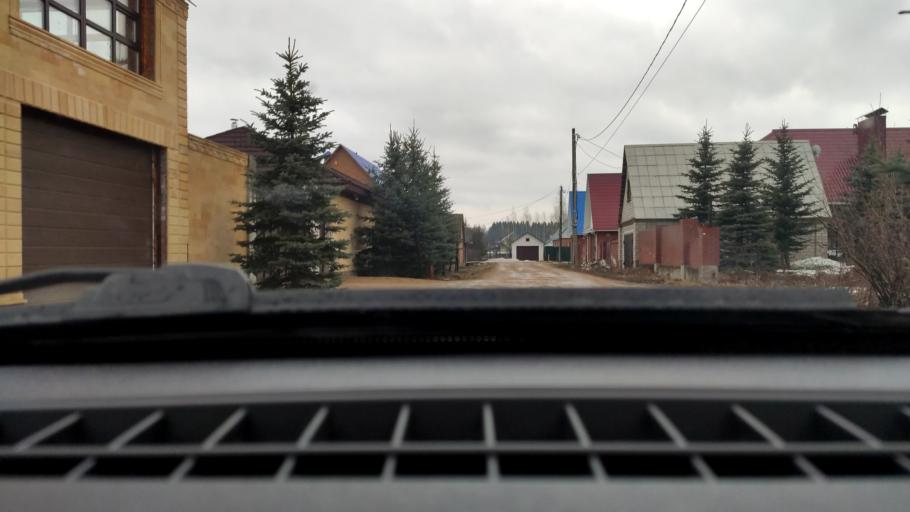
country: RU
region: Bashkortostan
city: Iglino
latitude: 54.8419
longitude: 56.2063
